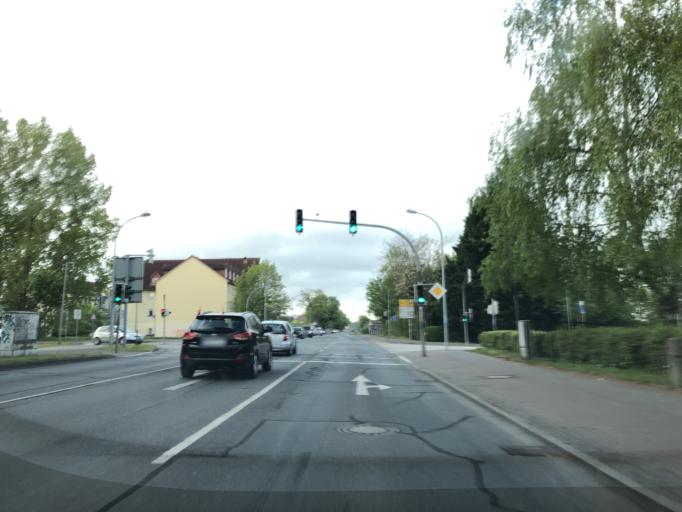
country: DE
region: Mecklenburg-Vorpommern
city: Guestrow
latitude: 53.7816
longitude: 12.1765
